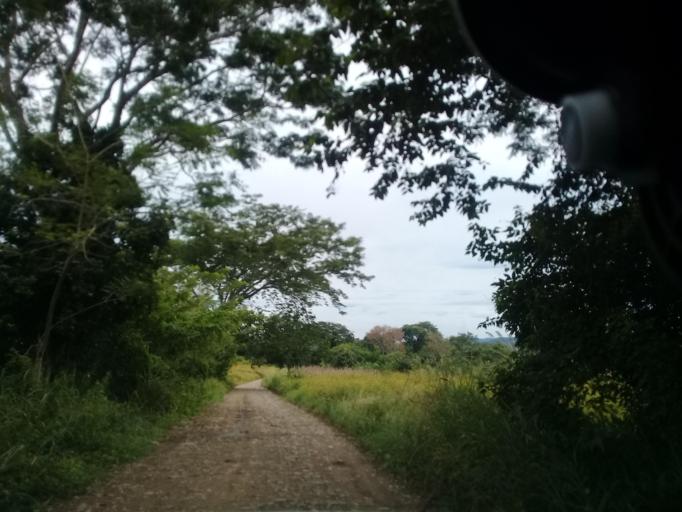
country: MX
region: Hidalgo
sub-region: Huejutla de Reyes
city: Chalahuiyapa
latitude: 21.1713
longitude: -98.3735
